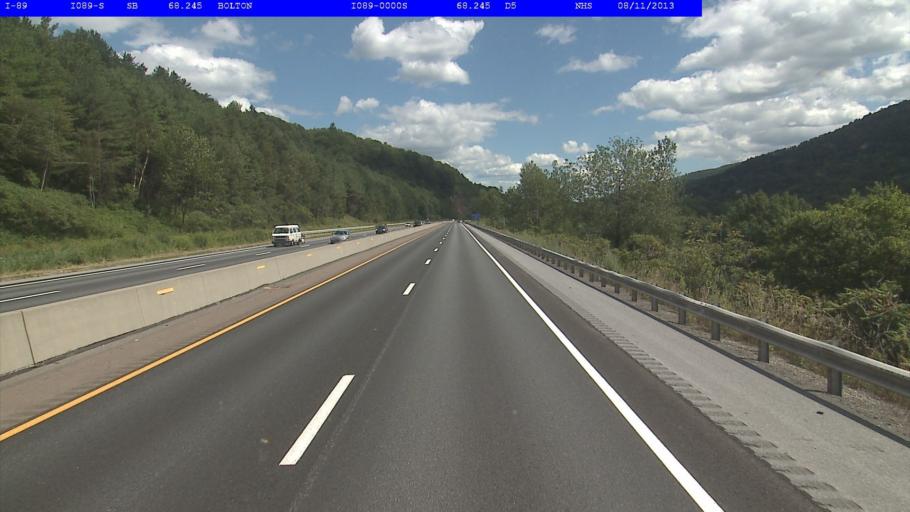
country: US
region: Vermont
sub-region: Washington County
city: Waterbury
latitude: 44.3618
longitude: -72.8346
